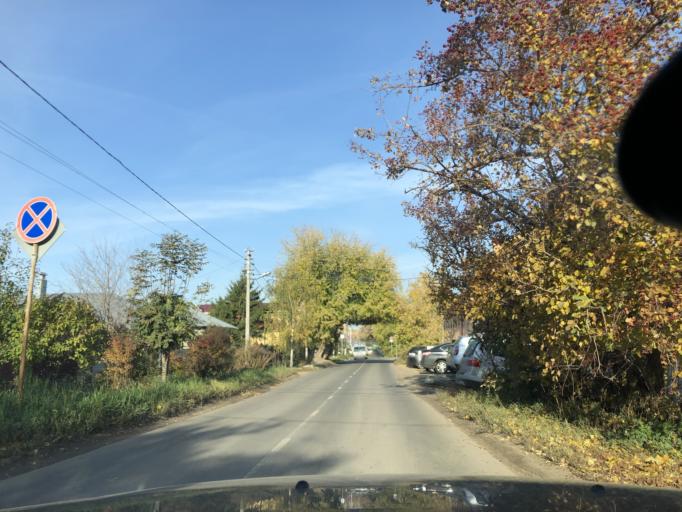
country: RU
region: Tula
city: Tula
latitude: 54.1901
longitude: 37.6309
